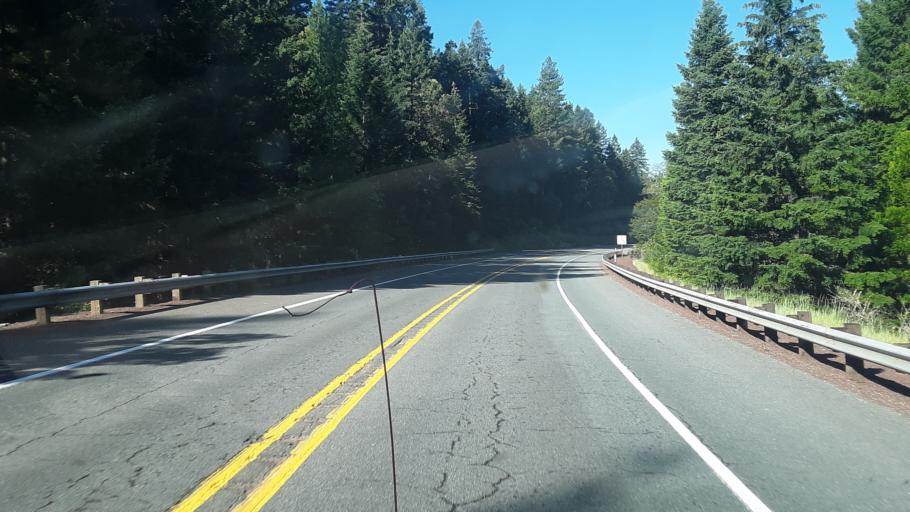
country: US
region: Oregon
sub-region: Jackson County
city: Shady Cove
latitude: 42.6756
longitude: -122.6218
